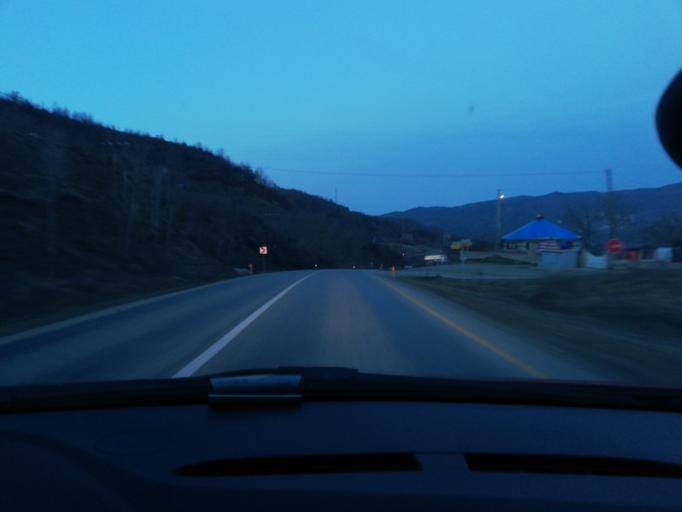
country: TR
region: Kastamonu
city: Inebolu
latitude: 41.9304
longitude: 33.7432
